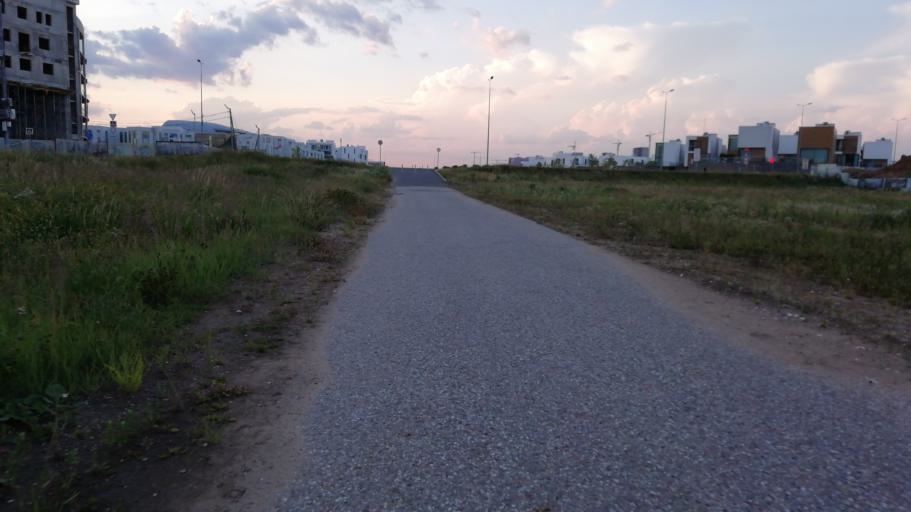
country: RU
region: Moskovskaya
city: Skolkovo
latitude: 55.6888
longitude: 37.3531
